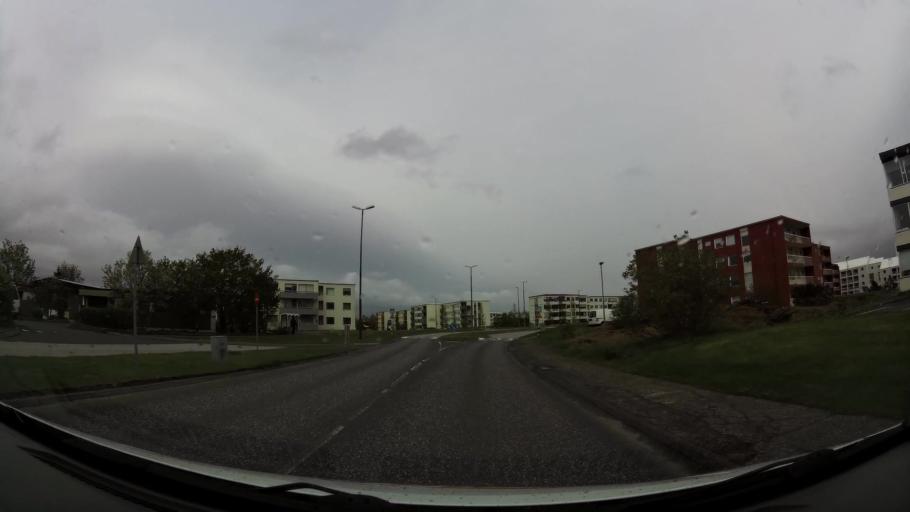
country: IS
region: Capital Region
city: Hafnarfjoerdur
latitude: 64.0790
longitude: -21.9635
